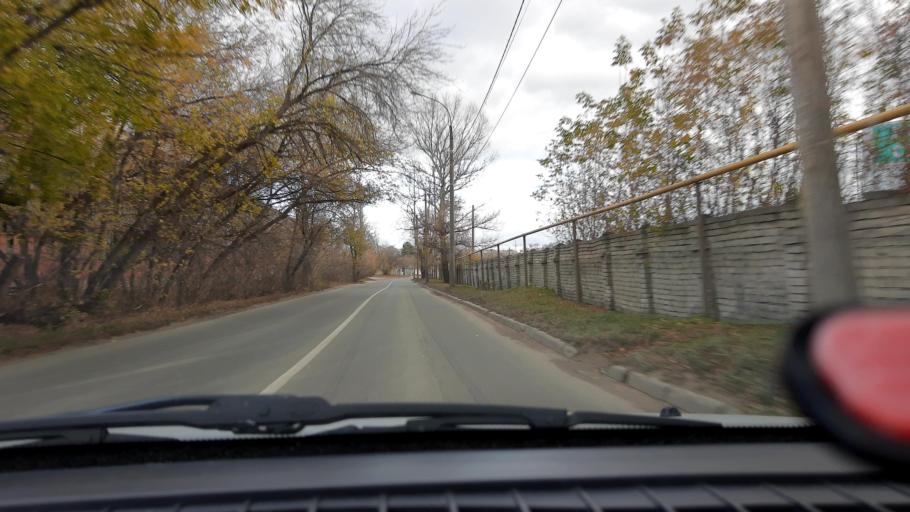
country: RU
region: Nizjnij Novgorod
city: Gorbatovka
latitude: 56.3472
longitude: 43.8195
